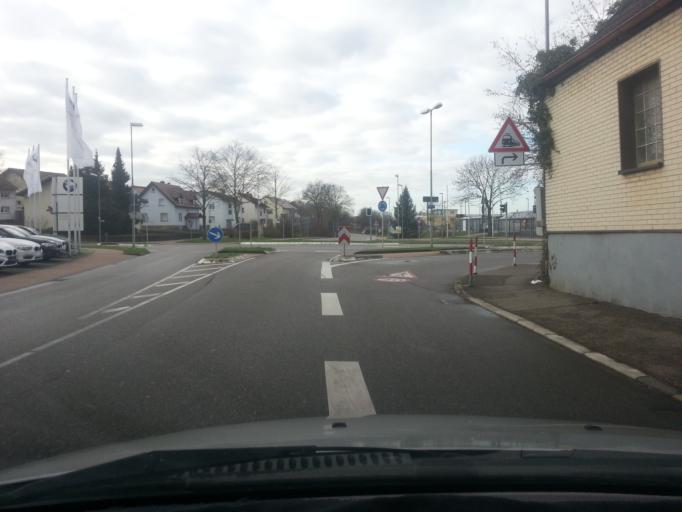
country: DE
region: Baden-Wuerttemberg
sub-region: Regierungsbezirk Stuttgart
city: Eppingen
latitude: 49.1327
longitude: 8.9061
